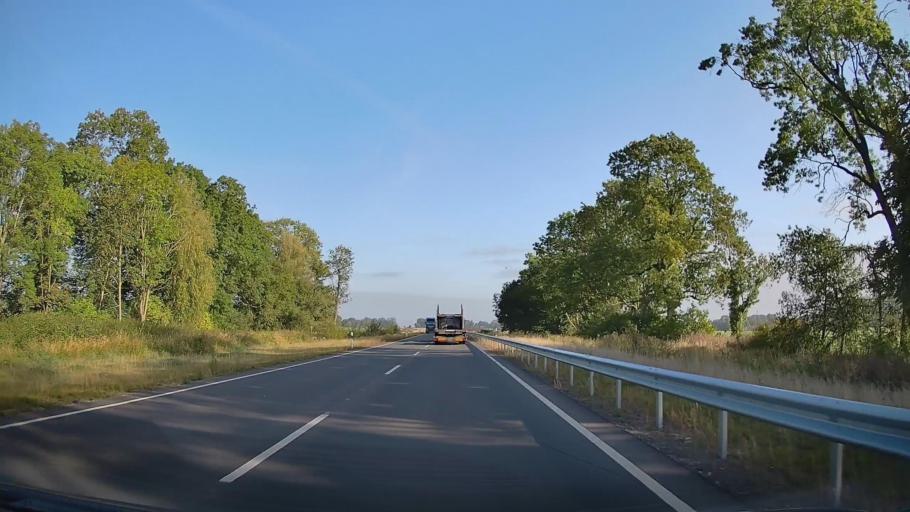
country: DE
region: Lower Saxony
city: Ovelgonne
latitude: 53.2979
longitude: 8.3958
